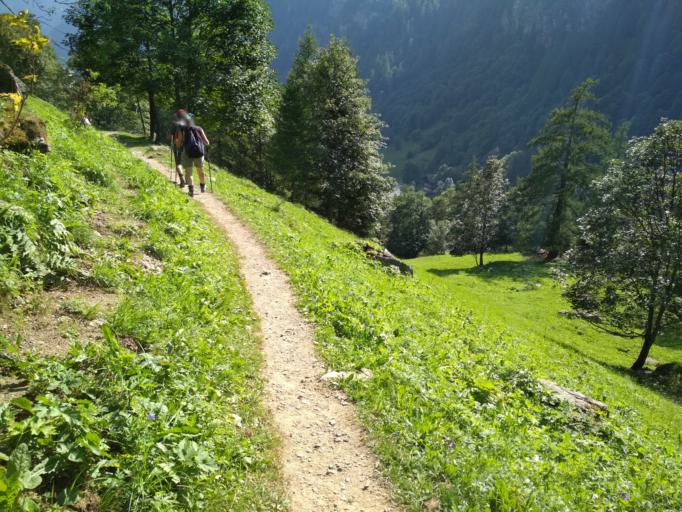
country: IT
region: Aosta Valley
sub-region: Valle d'Aosta
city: Gressoney-La-Trinite
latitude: 45.8036
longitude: 7.8266
